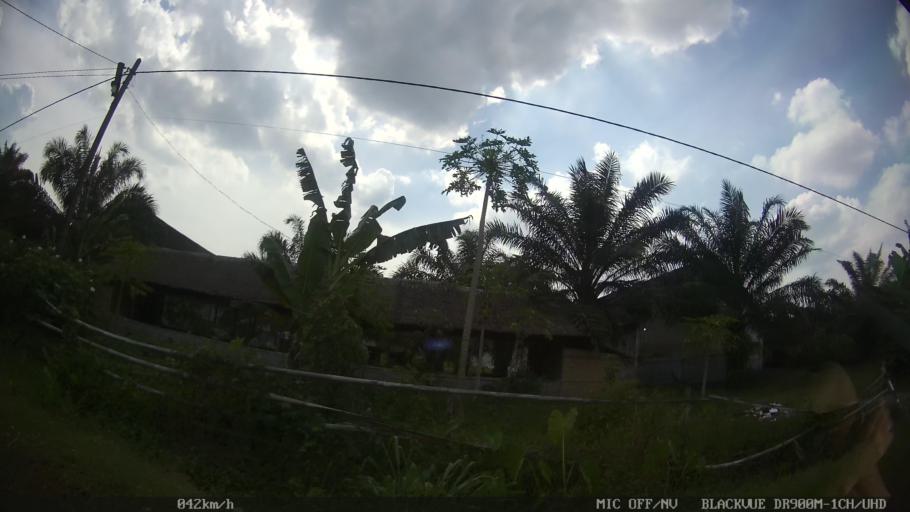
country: ID
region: North Sumatra
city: Binjai
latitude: 3.6341
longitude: 98.5173
